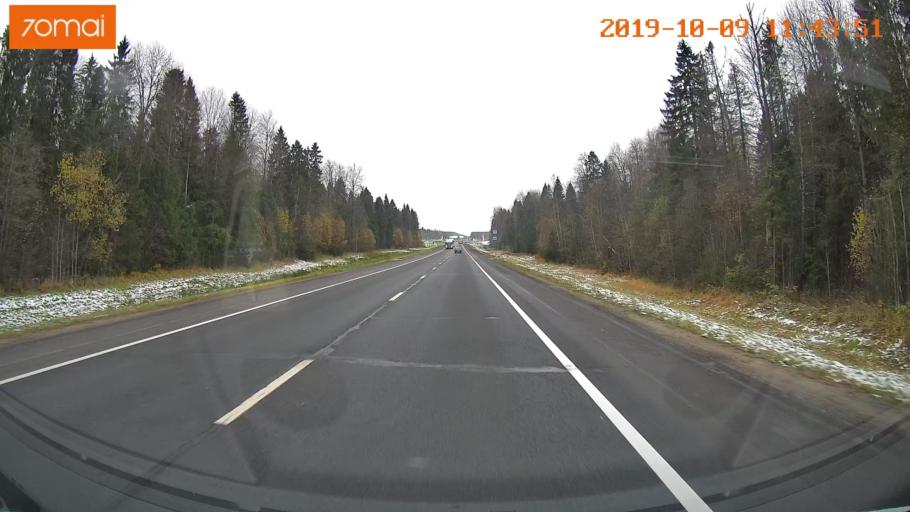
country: RU
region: Vologda
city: Gryazovets
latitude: 58.8911
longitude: 40.1881
